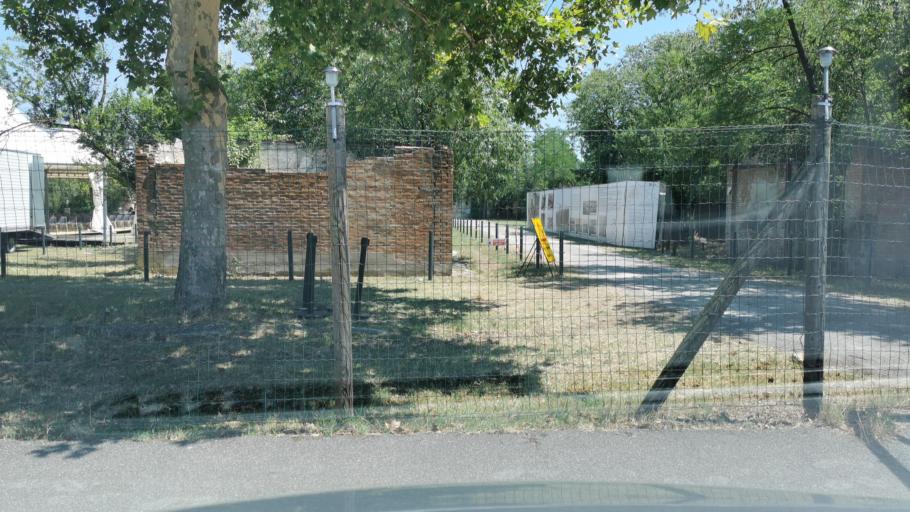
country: IT
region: Emilia-Romagna
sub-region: Provincia di Modena
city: Fossoli
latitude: 44.8280
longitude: 10.9014
